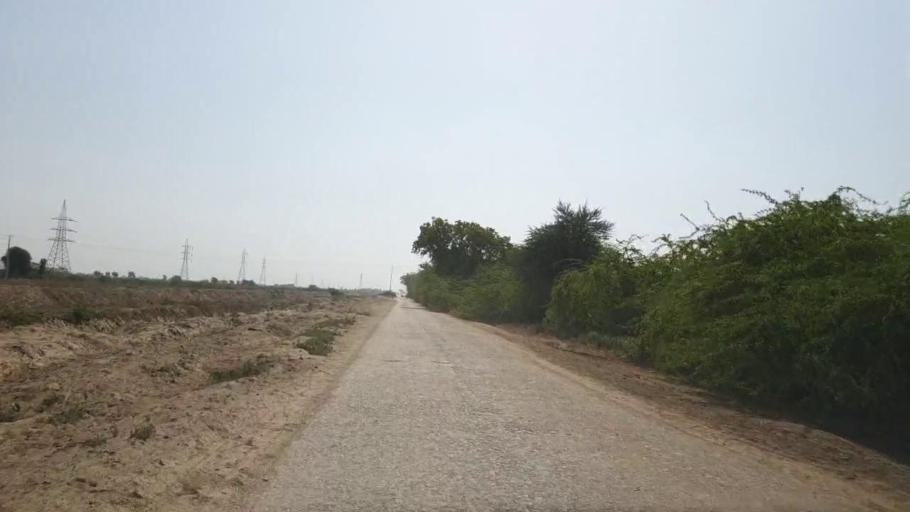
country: PK
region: Sindh
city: Naukot
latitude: 25.0102
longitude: 69.4583
